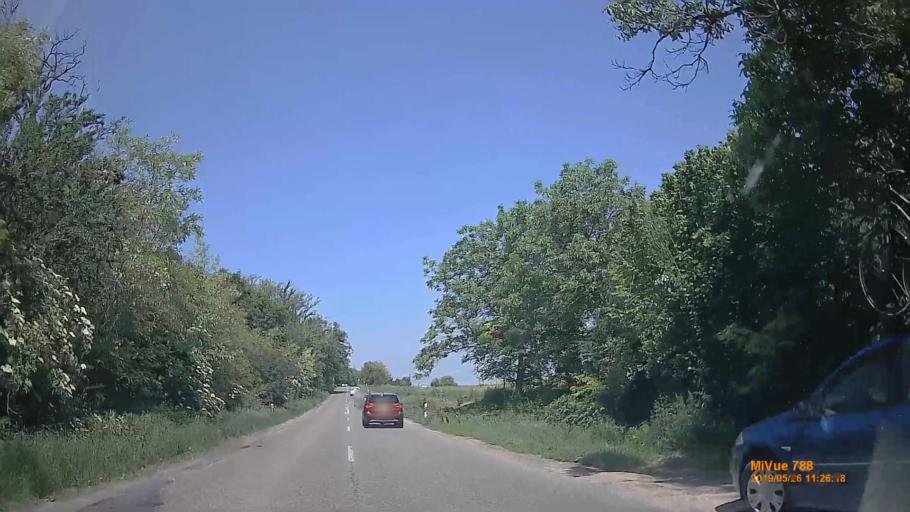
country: HU
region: Fejer
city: Lepseny
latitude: 46.9814
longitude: 18.1968
